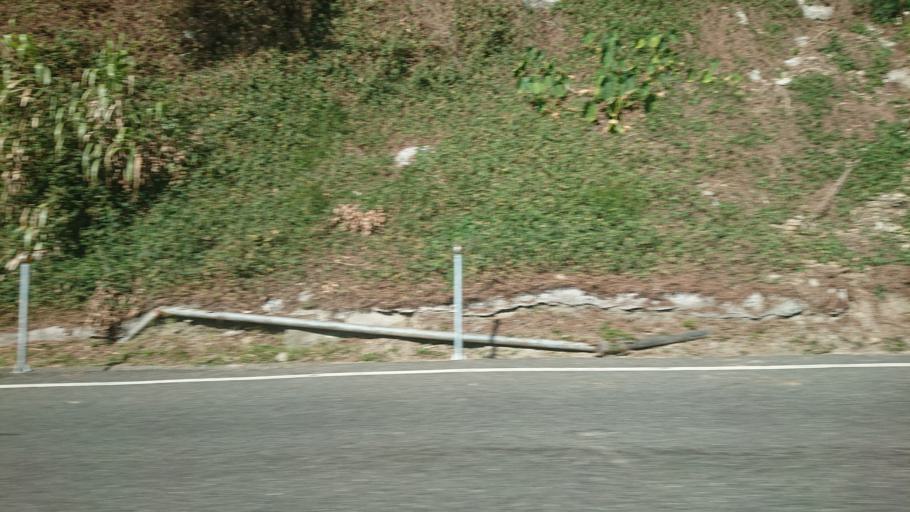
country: TW
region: Taiwan
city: Lugu
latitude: 23.4783
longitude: 120.7350
